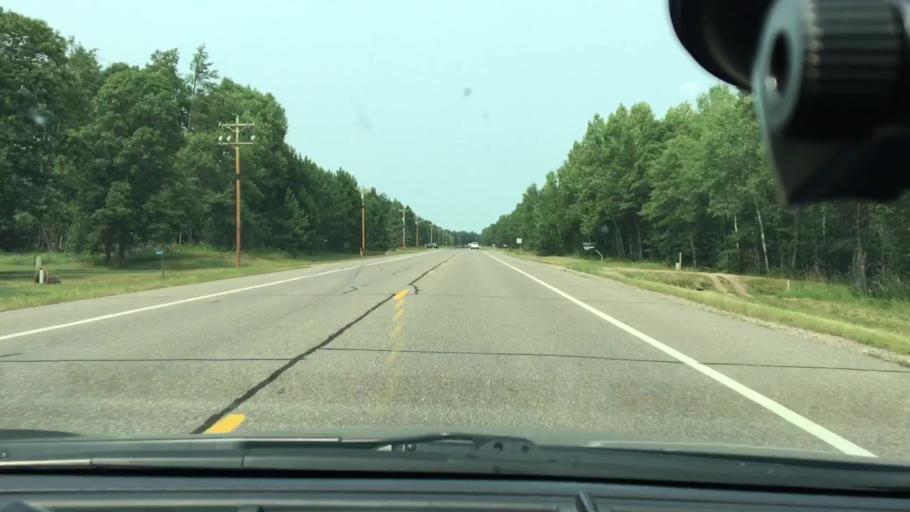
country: US
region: Minnesota
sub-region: Crow Wing County
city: Breezy Point
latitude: 46.5499
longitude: -94.1357
